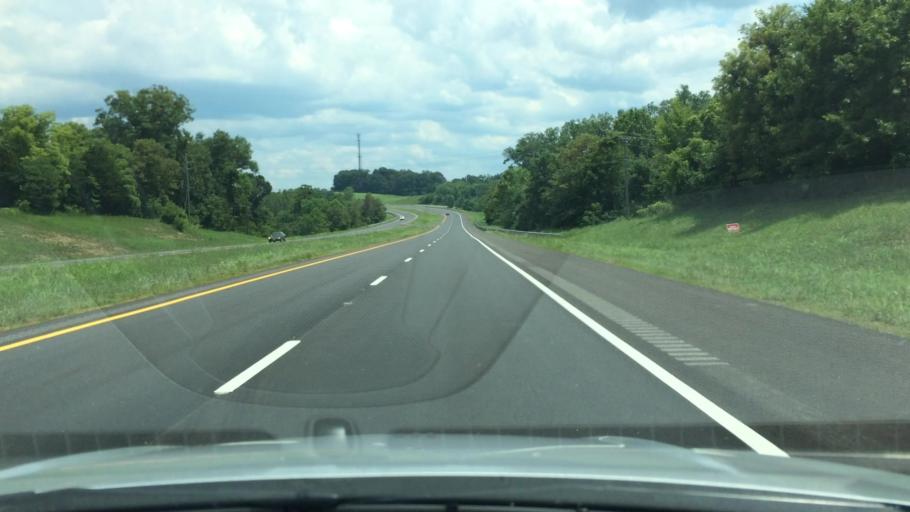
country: US
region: Tennessee
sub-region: Hamblen County
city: Morristown
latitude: 36.1771
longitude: -83.2328
